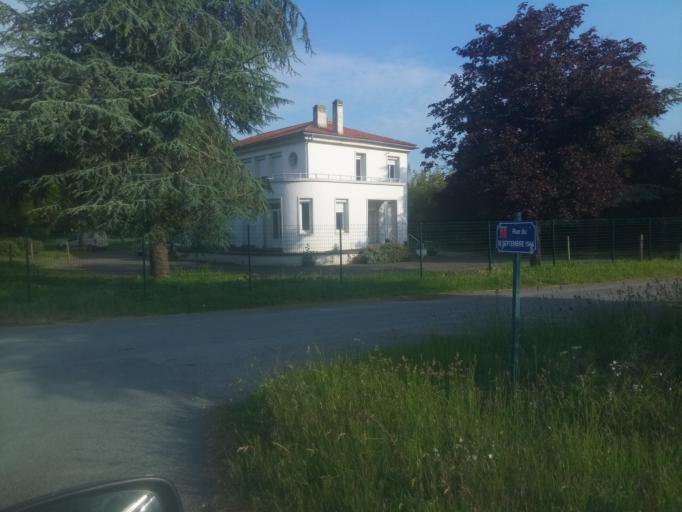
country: FR
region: Poitou-Charentes
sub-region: Departement de la Charente-Maritime
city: Saint-Jean-de-Liversay
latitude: 46.2255
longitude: -0.8806
